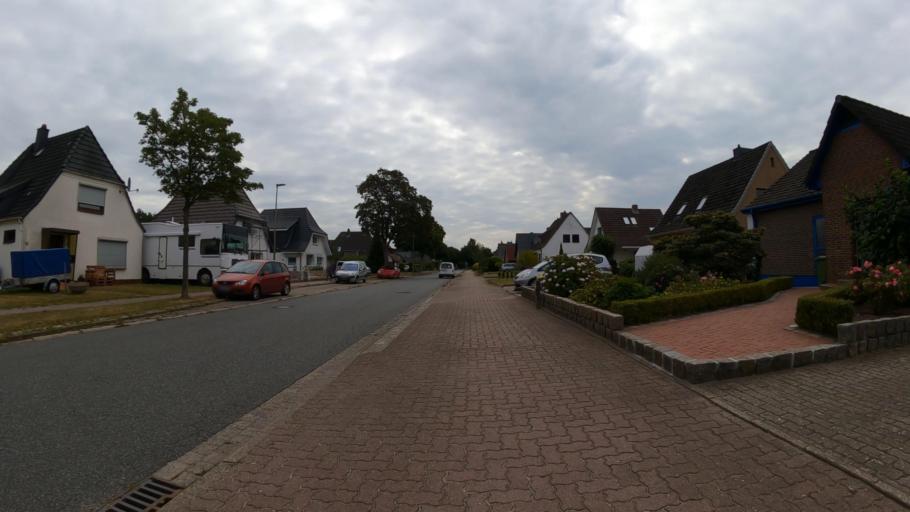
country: DE
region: Schleswig-Holstein
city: Boostedt
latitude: 54.0505
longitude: 10.0370
